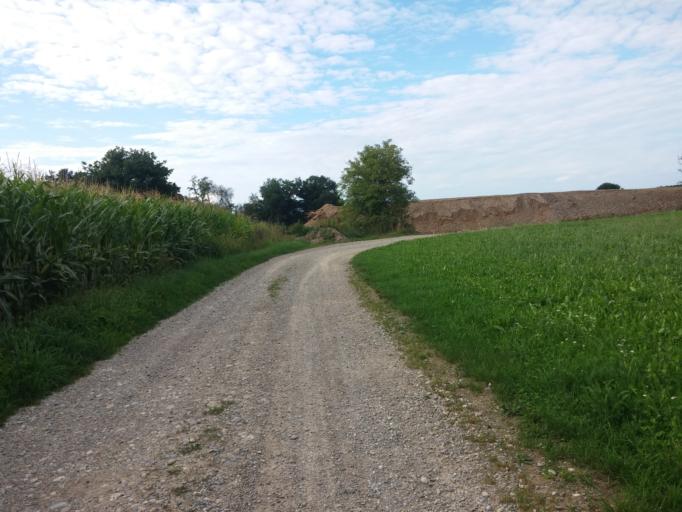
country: DE
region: Baden-Wuerttemberg
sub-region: Tuebingen Region
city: Aitrach
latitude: 47.9340
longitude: 10.0925
